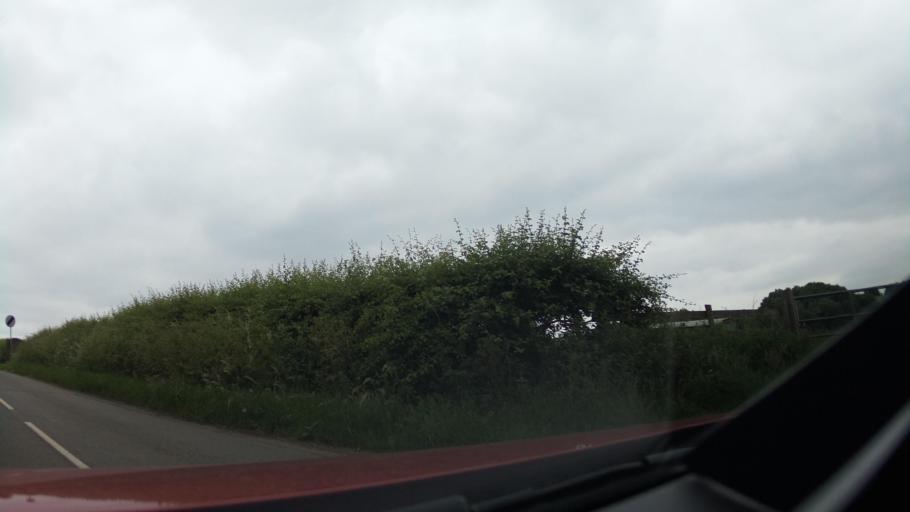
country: GB
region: England
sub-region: Leicestershire
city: Melton Mowbray
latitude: 52.6873
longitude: -0.8448
